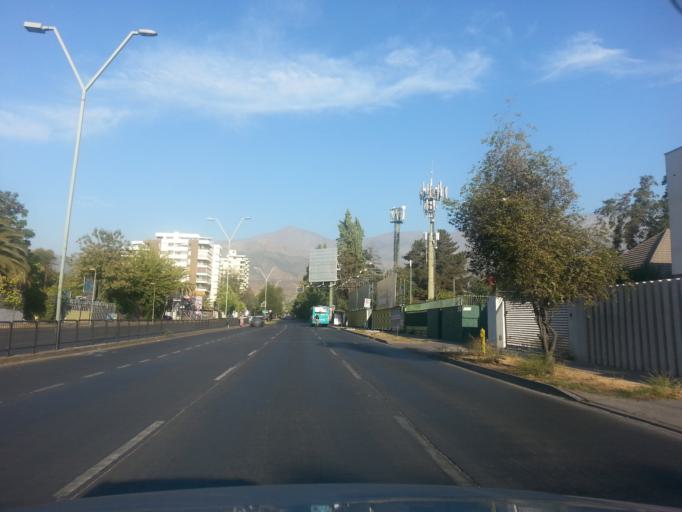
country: CL
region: Santiago Metropolitan
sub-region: Provincia de Santiago
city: Villa Presidente Frei, Nunoa, Santiago, Chile
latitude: -33.4311
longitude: -70.5664
